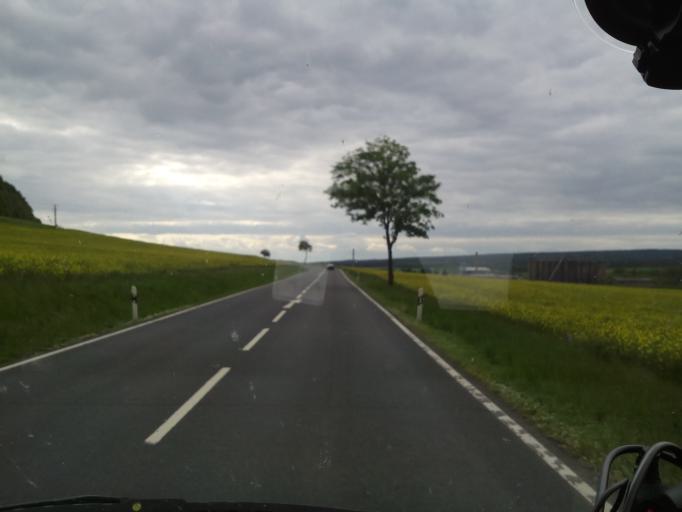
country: DE
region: Thuringia
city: Veilsdorf
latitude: 50.4130
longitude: 10.8396
